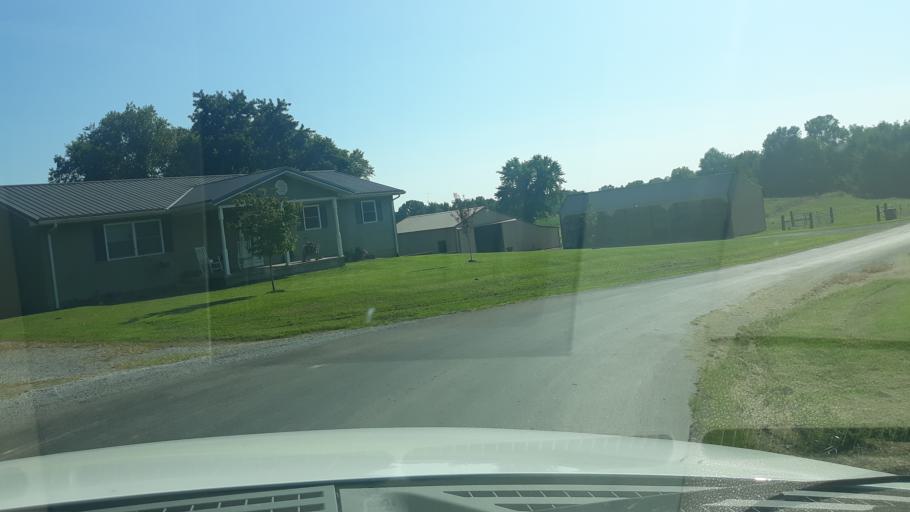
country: US
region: Illinois
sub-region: Saline County
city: Harrisburg
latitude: 37.8470
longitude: -88.6008
